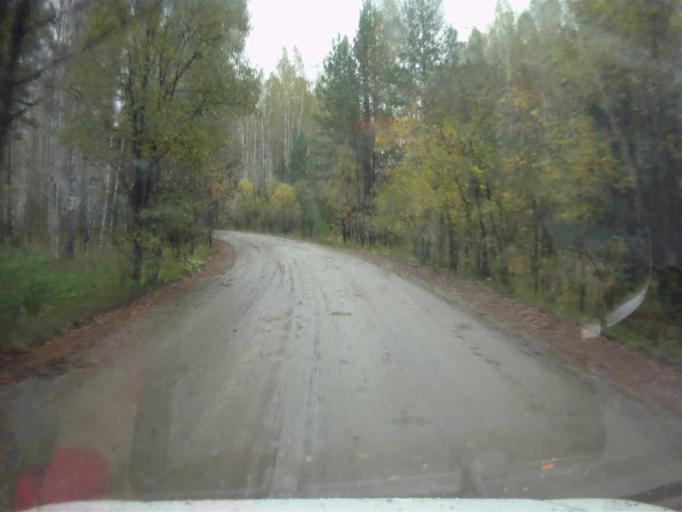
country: RU
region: Chelyabinsk
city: Kyshtym
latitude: 55.8410
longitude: 60.4867
